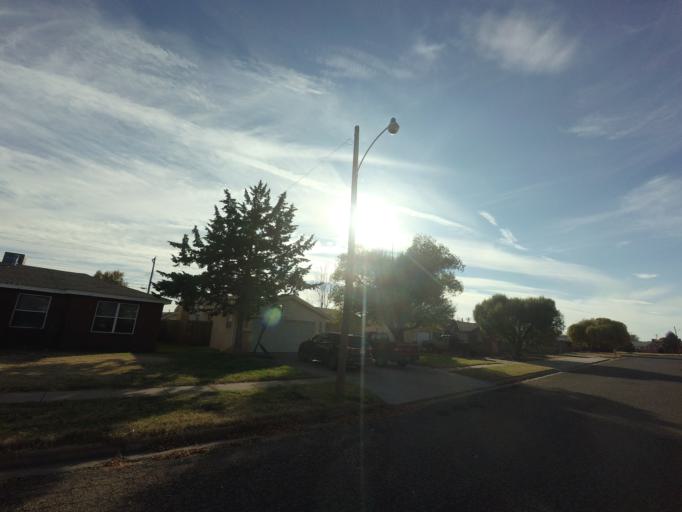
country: US
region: New Mexico
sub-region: Curry County
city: Clovis
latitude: 34.4230
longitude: -103.2163
